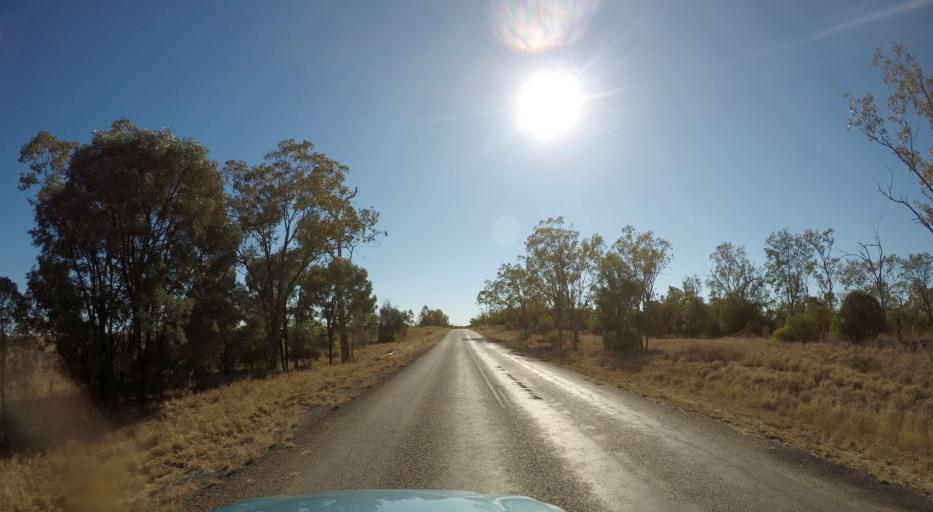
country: AU
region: Queensland
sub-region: Banana
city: Taroom
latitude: -26.0028
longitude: 149.3512
